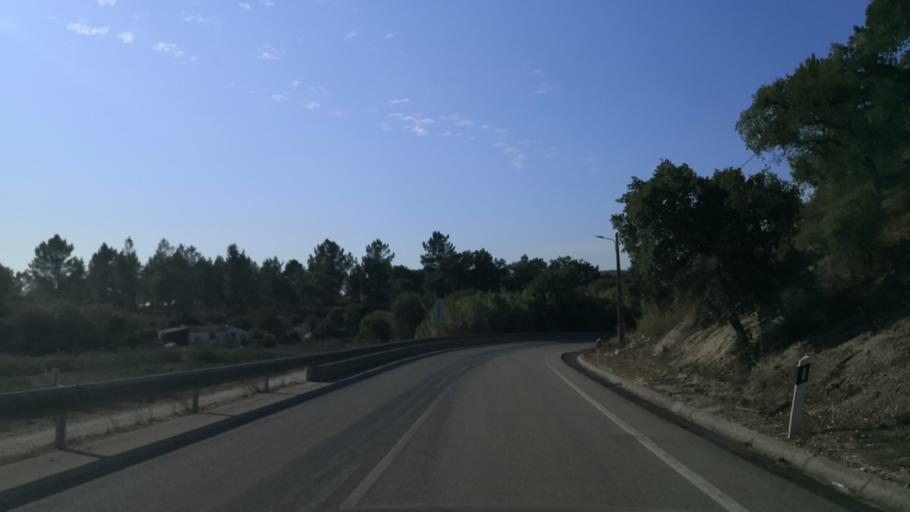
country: PT
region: Santarem
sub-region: Almeirim
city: Fazendas de Almeirim
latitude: 39.1056
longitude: -8.5798
